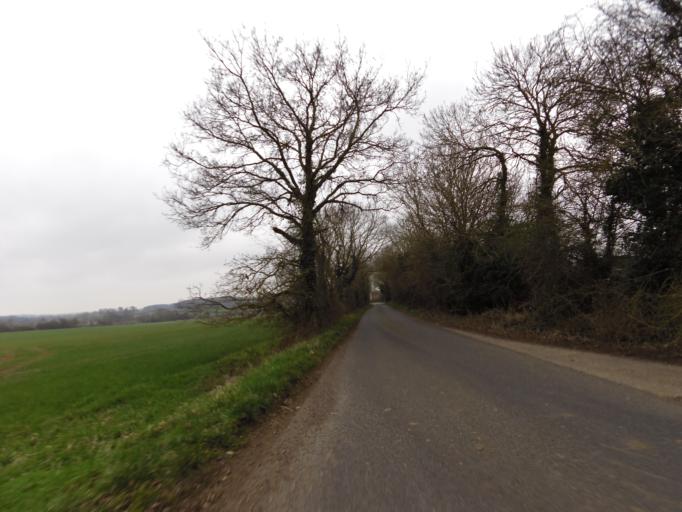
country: GB
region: England
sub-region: Suffolk
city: Framlingham
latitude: 52.2118
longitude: 1.3276
